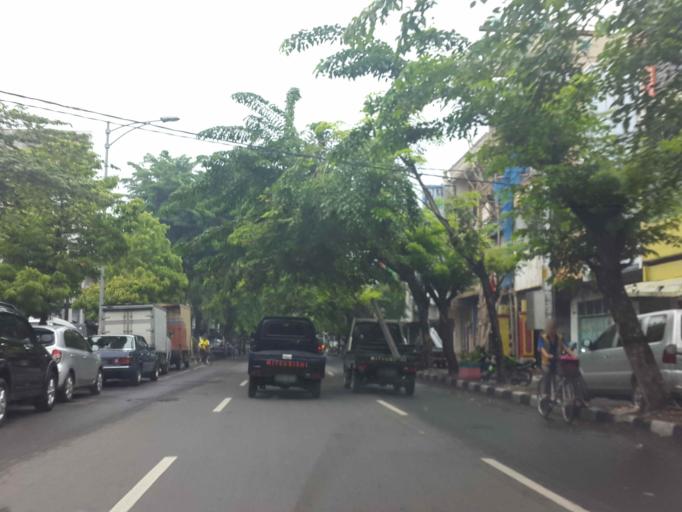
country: ID
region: Central Java
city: Semarang
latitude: -6.9755
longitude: 110.4312
